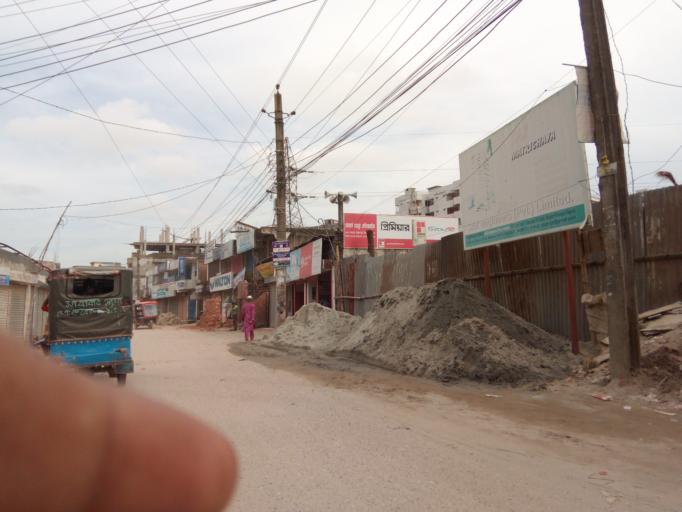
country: BD
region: Dhaka
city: Tungi
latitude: 23.8445
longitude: 90.4216
